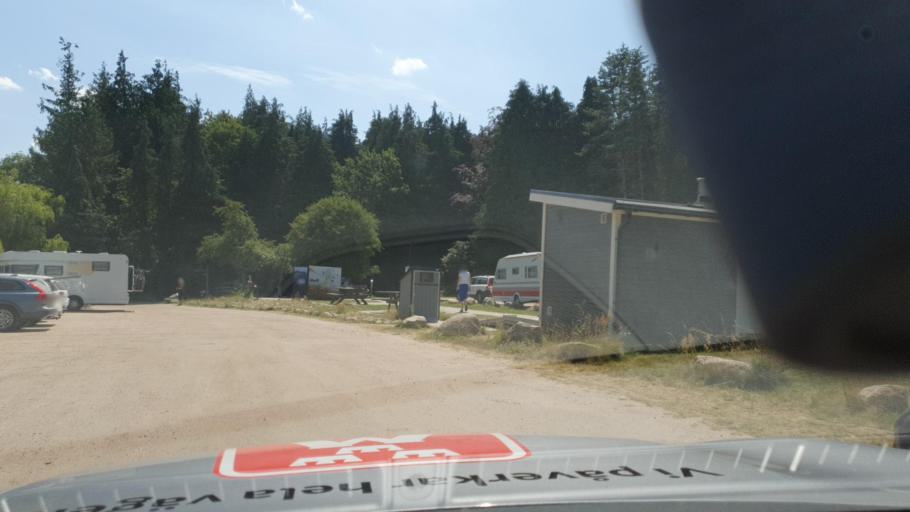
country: SE
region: Skane
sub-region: Simrishamns Kommun
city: Kivik
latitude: 55.6714
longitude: 14.2676
